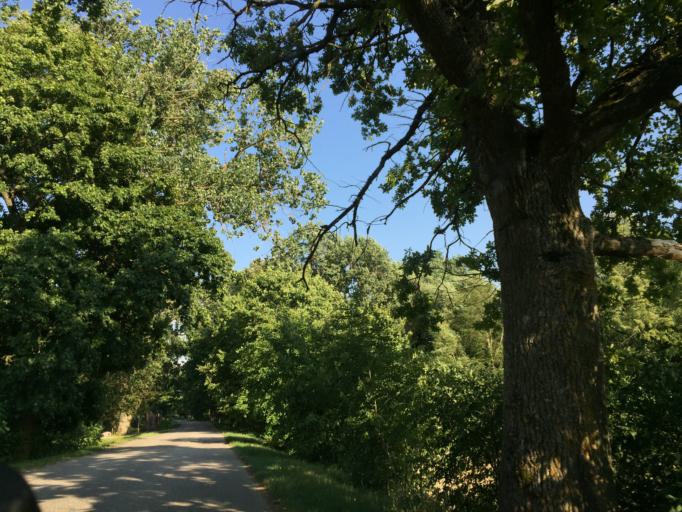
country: LT
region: Siauliu apskritis
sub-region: Joniskis
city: Joniskis
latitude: 56.4234
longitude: 23.6951
